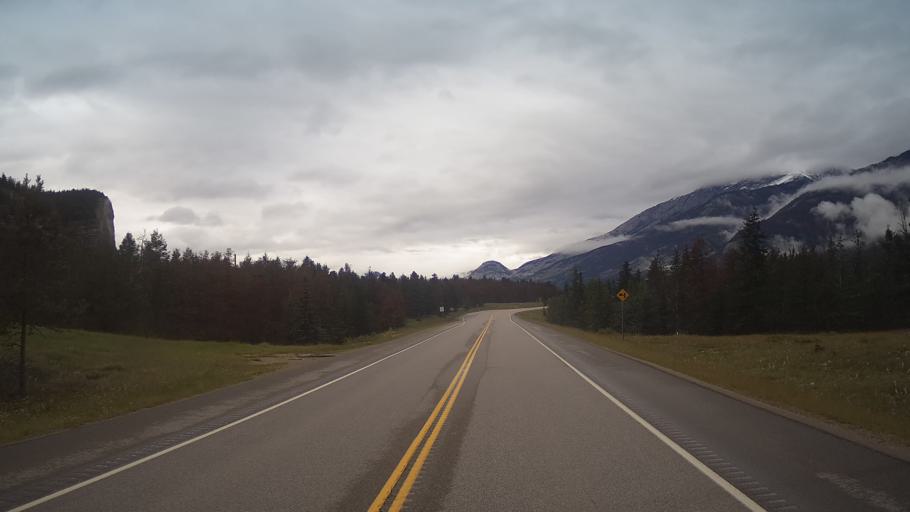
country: CA
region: Alberta
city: Jasper Park Lodge
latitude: 52.9361
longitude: -118.0387
